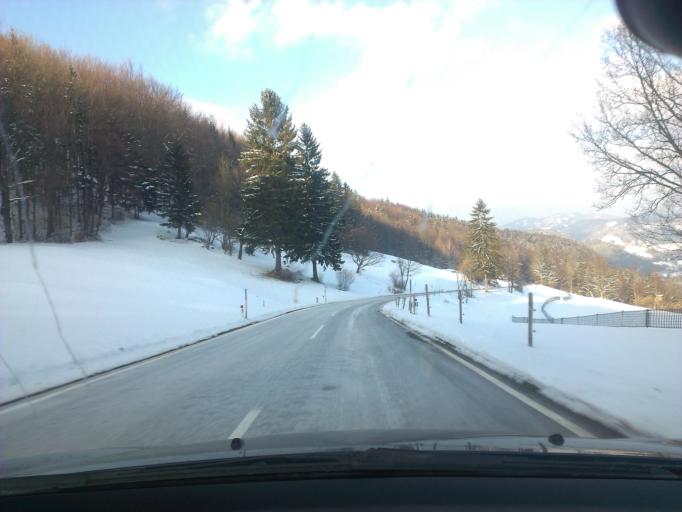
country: AT
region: Lower Austria
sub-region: Politischer Bezirk Neunkirchen
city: Puchberg am Schneeberg
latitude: 47.8150
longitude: 15.9421
